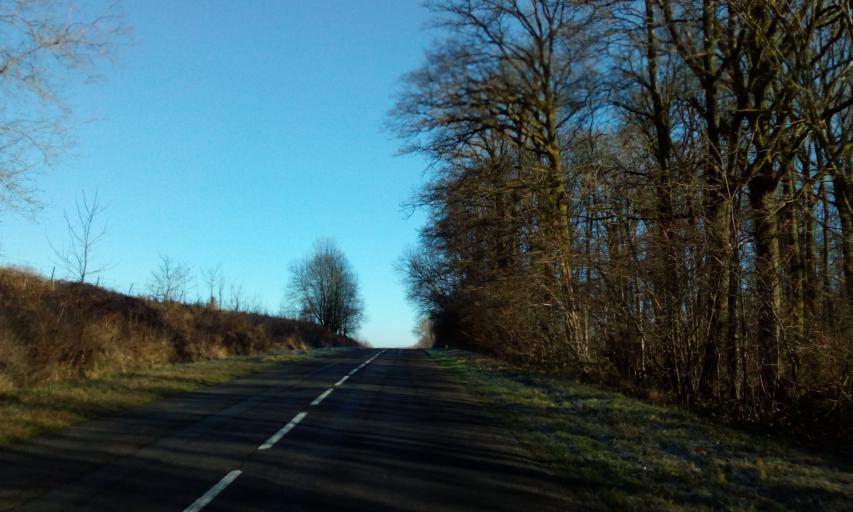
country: FR
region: Champagne-Ardenne
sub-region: Departement des Ardennes
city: Signy-le-Petit
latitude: 49.7774
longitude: 4.3602
